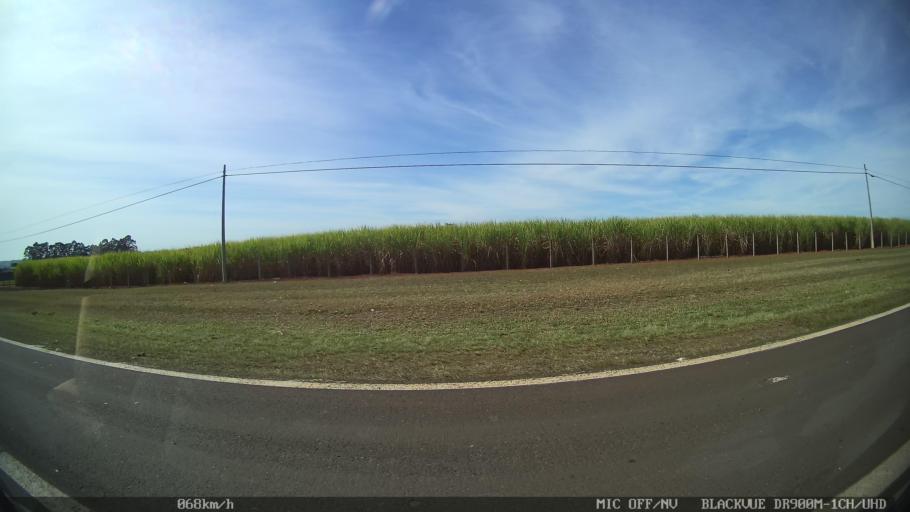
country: BR
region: Sao Paulo
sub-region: Piracicaba
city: Piracicaba
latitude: -22.7793
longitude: -47.6514
